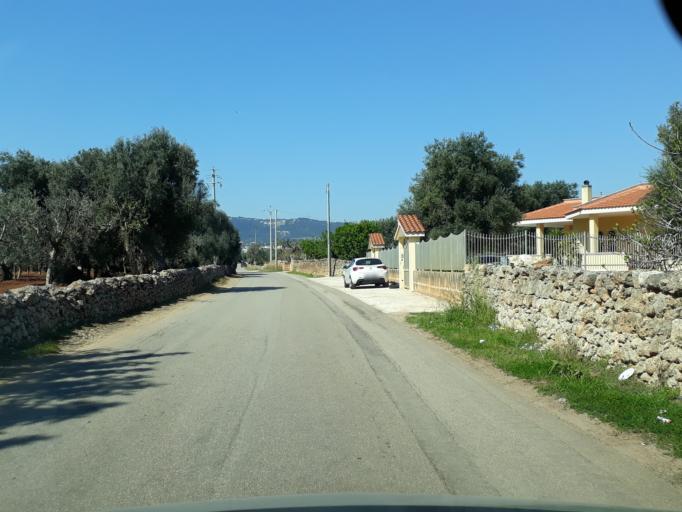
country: IT
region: Apulia
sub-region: Provincia di Brindisi
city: Fasano
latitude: 40.8351
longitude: 17.3779
